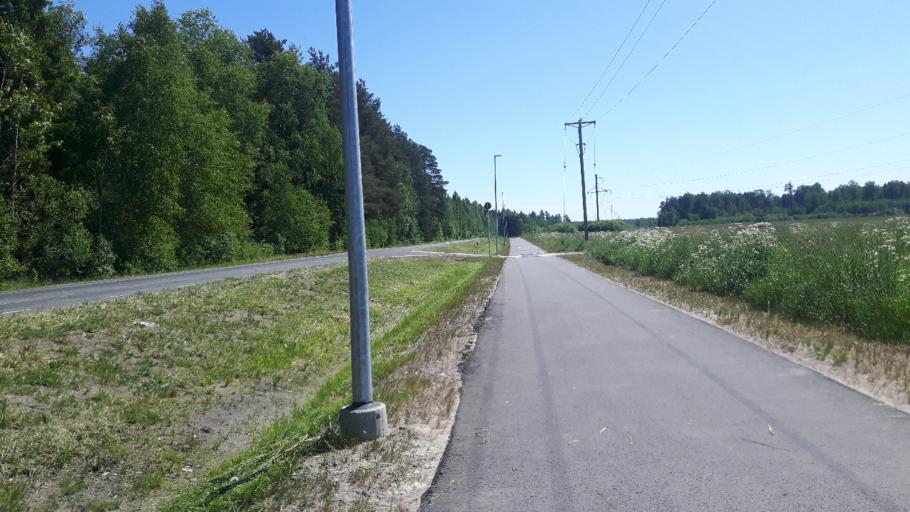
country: EE
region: Raplamaa
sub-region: Kohila vald
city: Kohila
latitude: 59.2112
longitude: 24.6824
